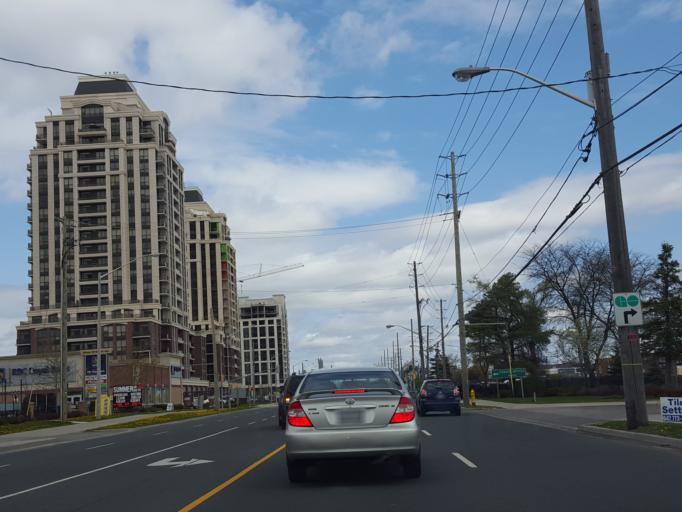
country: CA
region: Ontario
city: Markham
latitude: 43.8947
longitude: -79.2647
